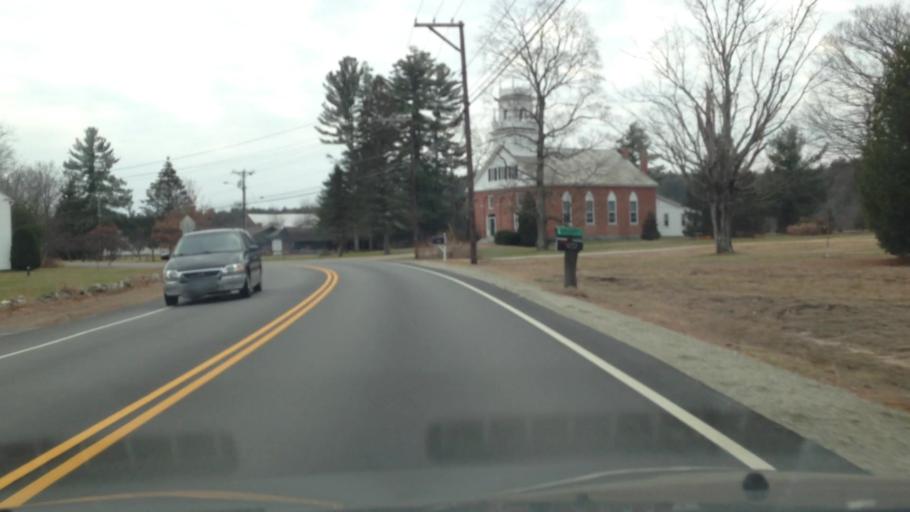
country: US
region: New Hampshire
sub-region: Cheshire County
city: Swanzey
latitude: 42.8697
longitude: -72.2826
